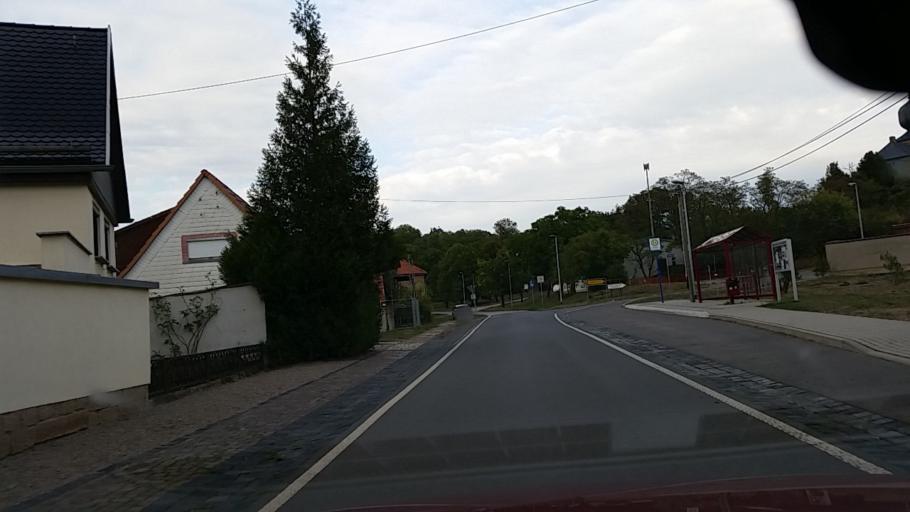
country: DE
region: Thuringia
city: Beichlingen
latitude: 51.2305
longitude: 11.2539
